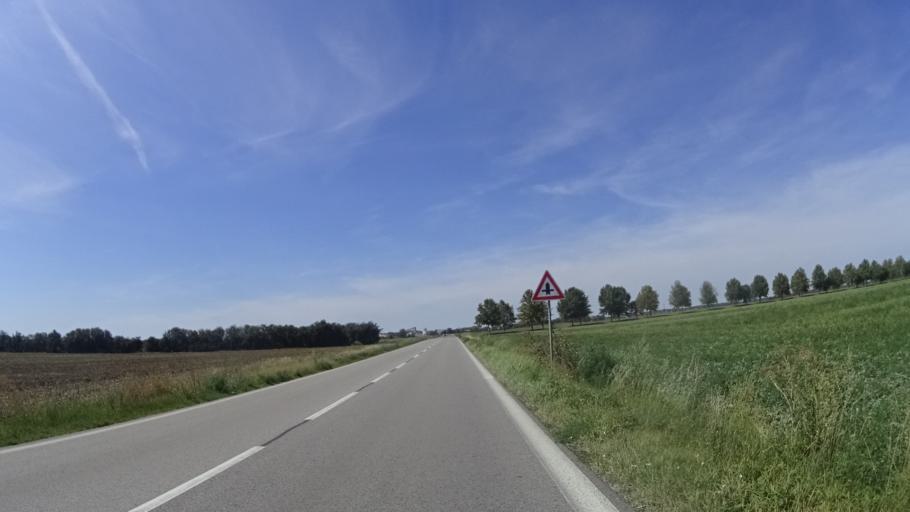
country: AT
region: Lower Austria
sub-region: Politischer Bezirk Ganserndorf
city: Marchegg
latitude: 48.3078
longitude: 16.9382
